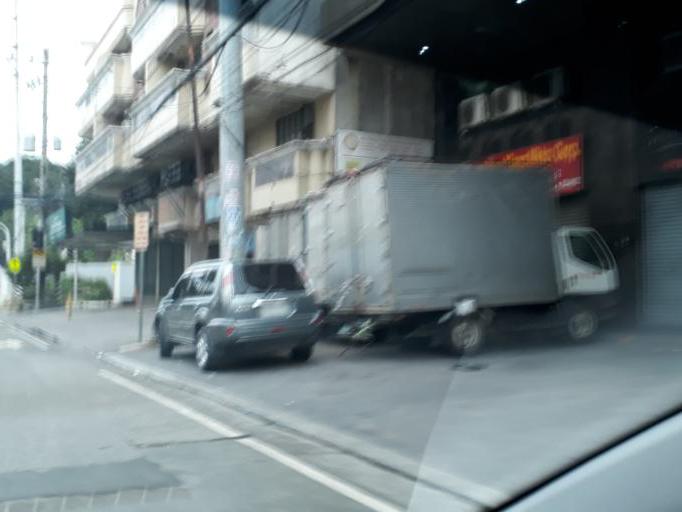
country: PH
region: Calabarzon
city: Del Monte
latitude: 14.6258
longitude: 121.0016
